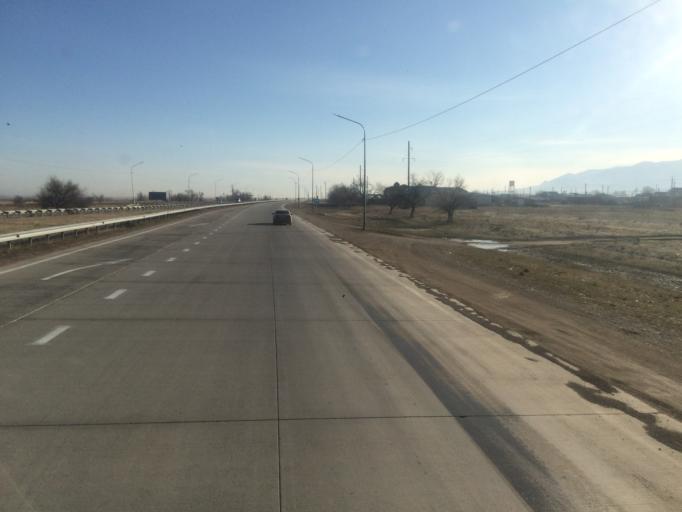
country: KZ
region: Zhambyl
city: Sarykemer
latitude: 43.0091
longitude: 71.7935
